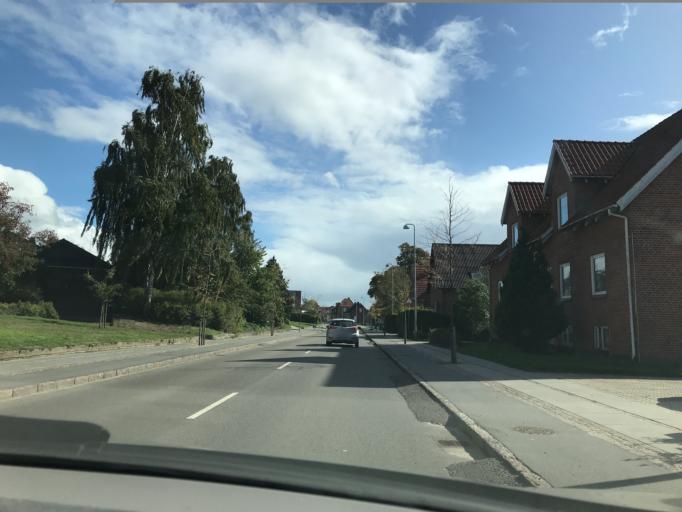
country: DK
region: Central Jutland
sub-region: Skanderborg Kommune
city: Skanderborg
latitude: 56.0340
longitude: 9.9236
